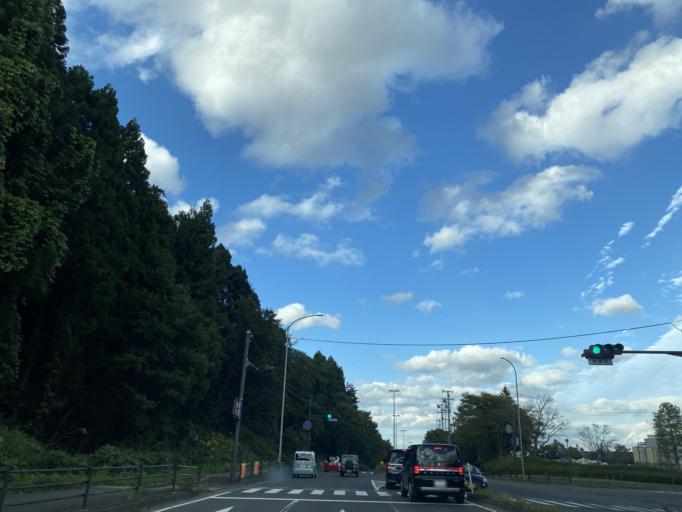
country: JP
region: Miyagi
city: Tomiya
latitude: 38.3549
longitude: 140.8434
